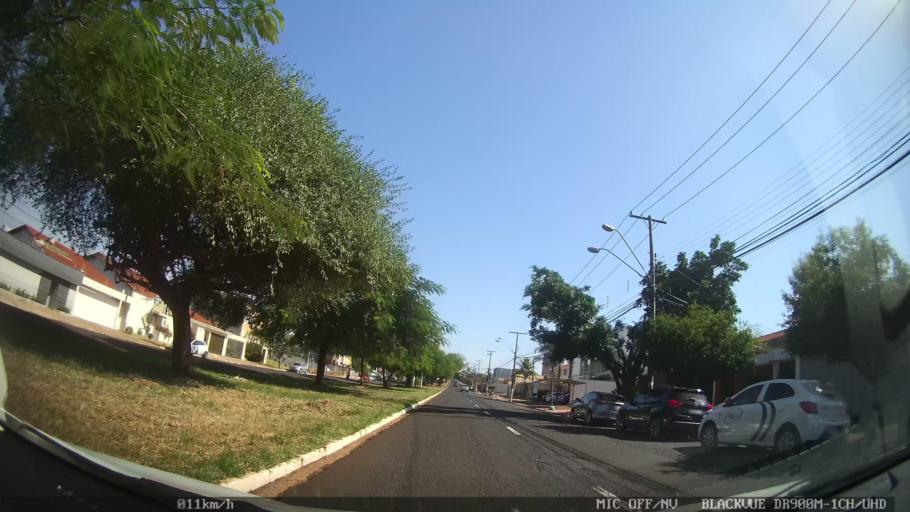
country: BR
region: Sao Paulo
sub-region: Ribeirao Preto
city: Ribeirao Preto
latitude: -21.2053
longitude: -47.7714
